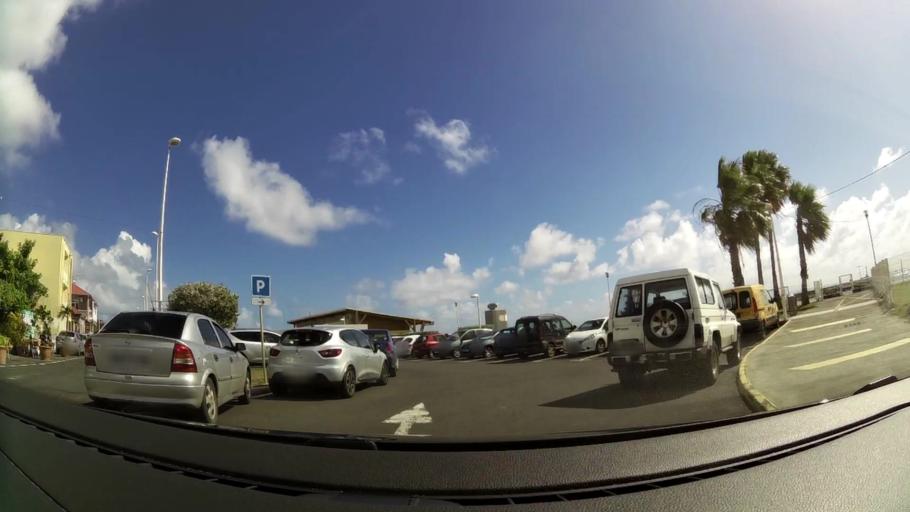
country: GP
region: Guadeloupe
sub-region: Guadeloupe
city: Saint-Francois
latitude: 16.2506
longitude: -61.2736
